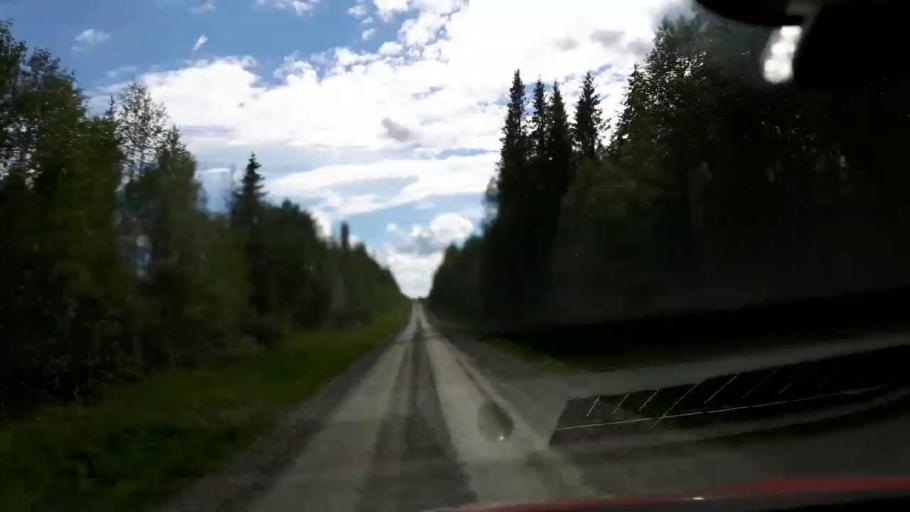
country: SE
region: Jaemtland
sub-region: Krokoms Kommun
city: Valla
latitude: 63.8909
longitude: 14.1590
